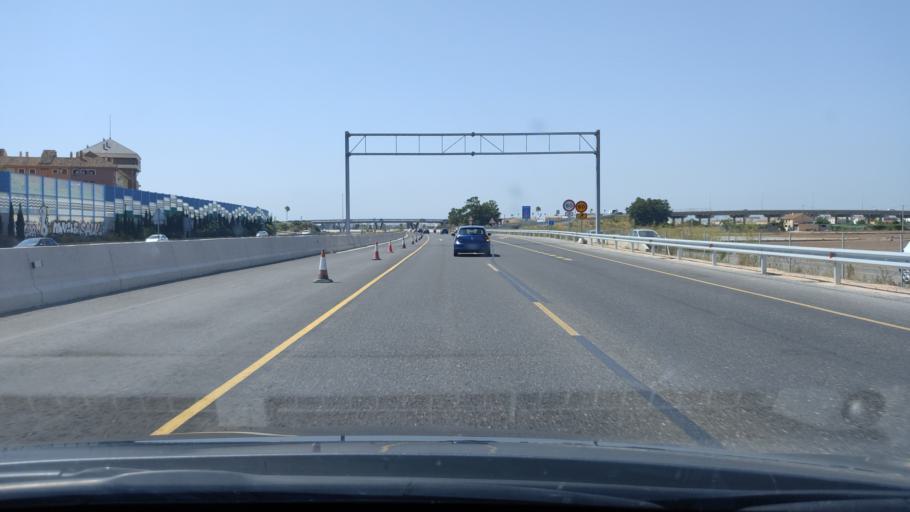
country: ES
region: Valencia
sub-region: Provincia de Valencia
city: Meliana
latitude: 39.5117
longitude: -0.3233
